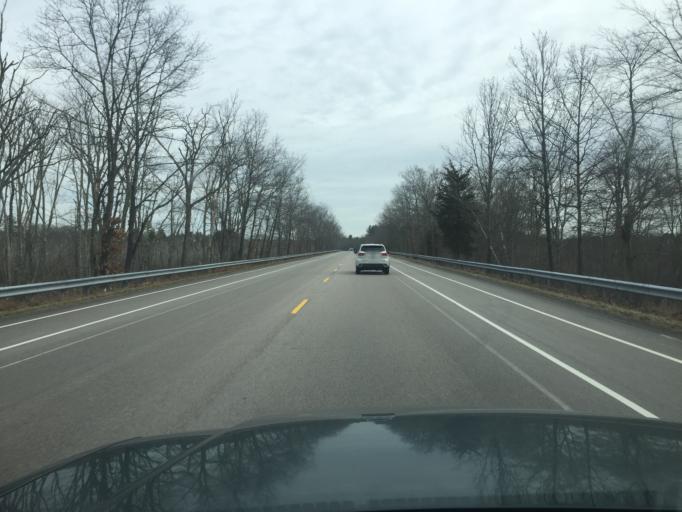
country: US
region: Massachusetts
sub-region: Norfolk County
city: Medfield
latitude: 42.2036
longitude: -71.3377
